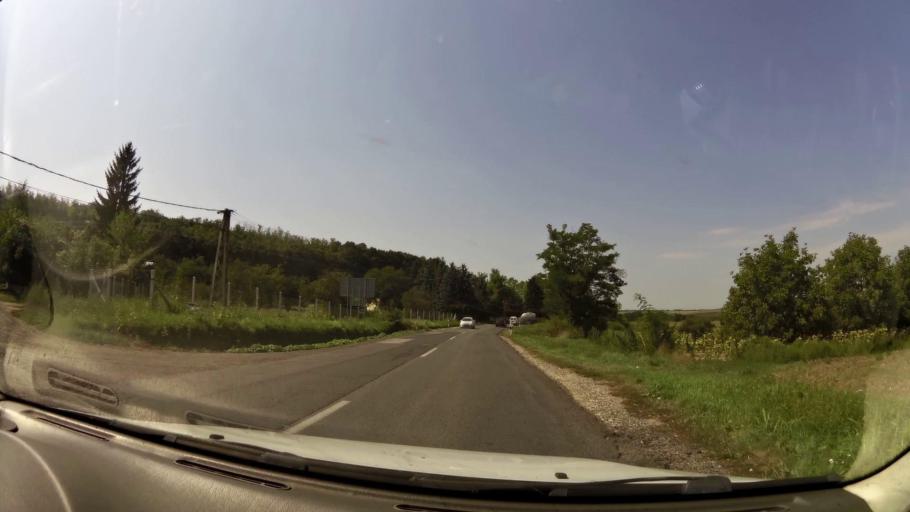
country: HU
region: Pest
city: Suelysap
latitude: 47.4463
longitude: 19.5135
